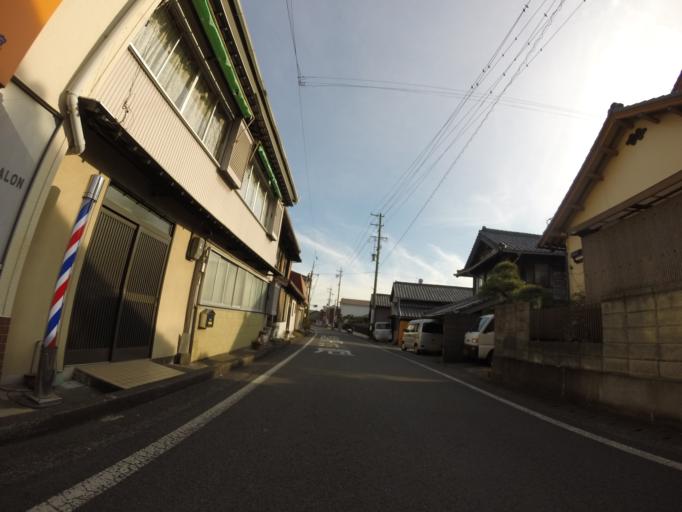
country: JP
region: Shizuoka
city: Shizuoka-shi
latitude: 35.0528
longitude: 138.4763
